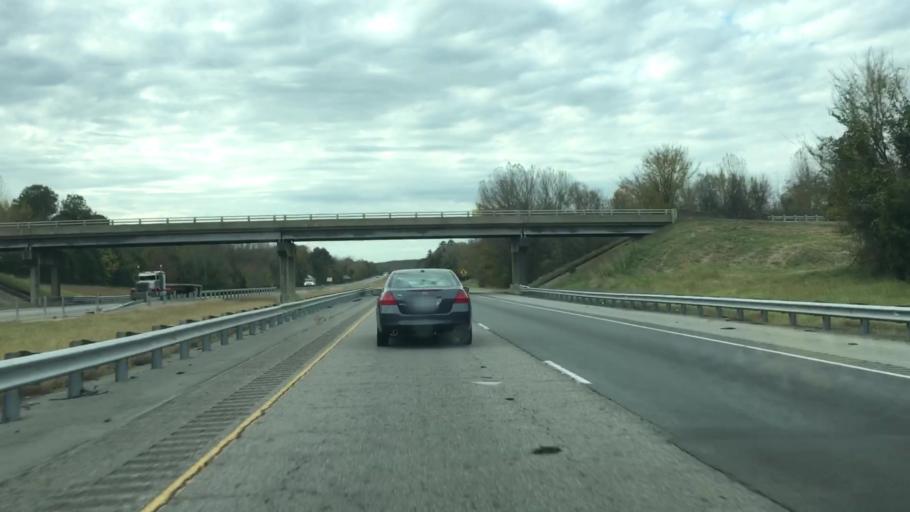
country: US
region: Arkansas
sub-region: Faulkner County
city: Conway
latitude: 35.1531
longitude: -92.5528
